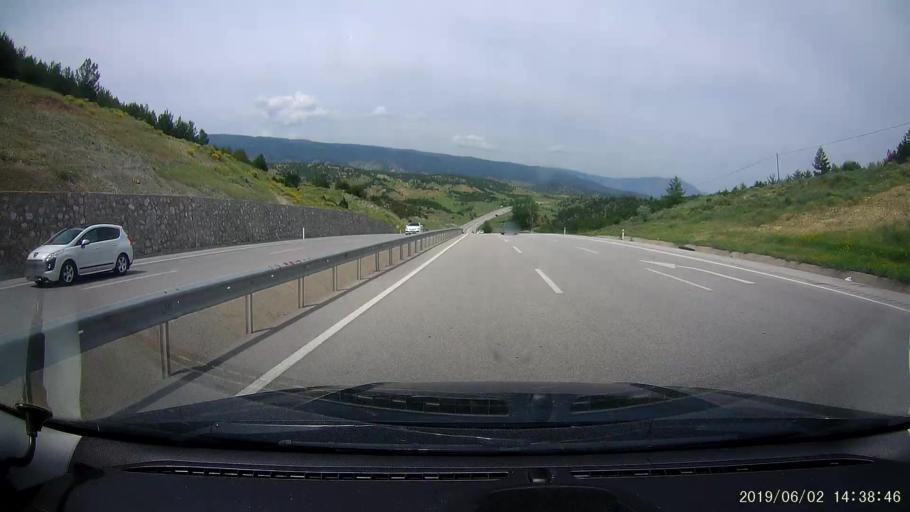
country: TR
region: Corum
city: Hacihamza
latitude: 41.0601
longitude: 34.2879
